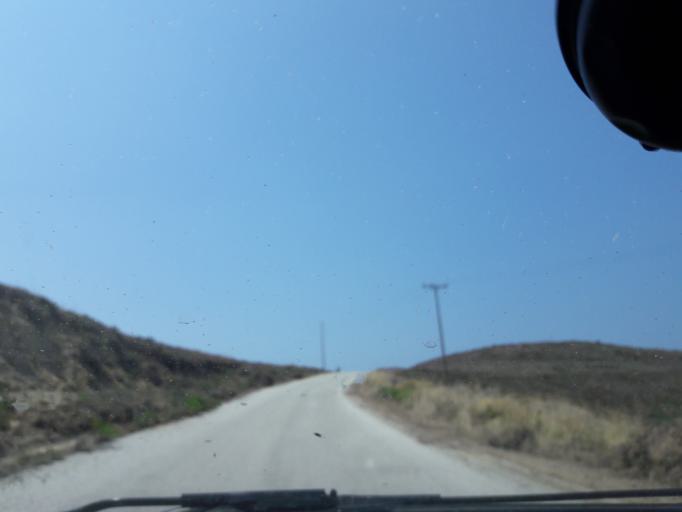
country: GR
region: North Aegean
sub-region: Nomos Lesvou
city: Myrina
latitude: 39.9755
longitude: 25.3518
